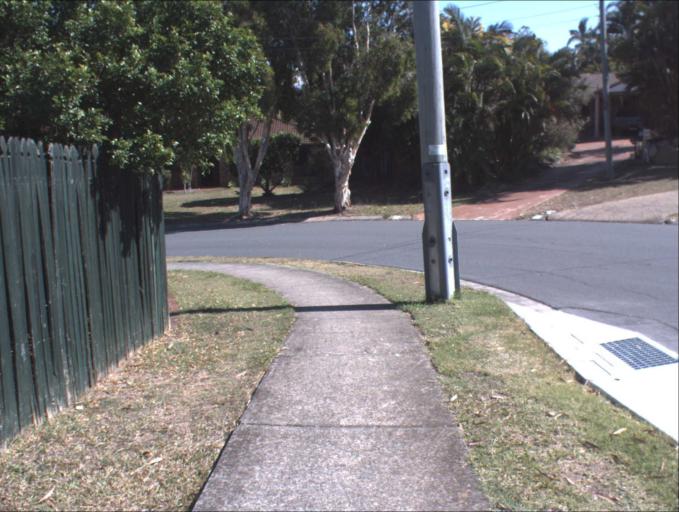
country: AU
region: Queensland
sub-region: Logan
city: Rochedale South
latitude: -27.5958
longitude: 153.1334
